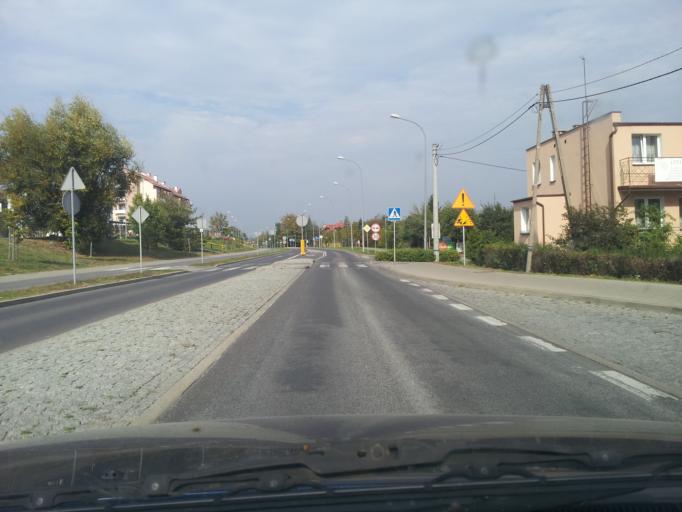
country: PL
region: Warmian-Masurian Voivodeship
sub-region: Powiat ilawski
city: Ilawa
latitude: 53.6054
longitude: 19.5676
